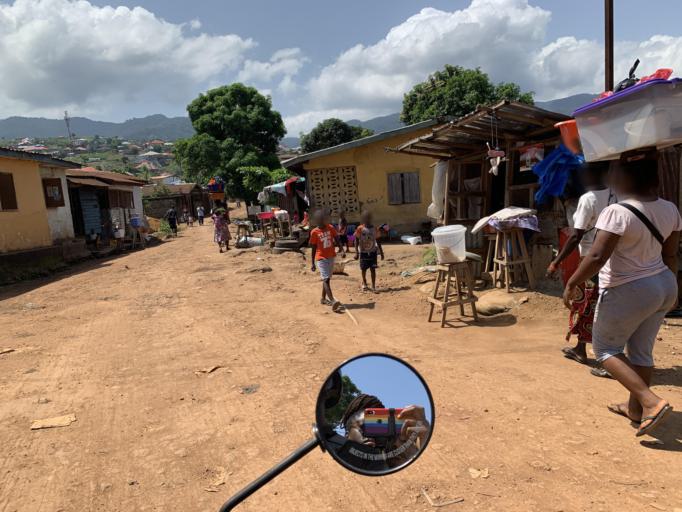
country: SL
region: Western Area
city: Hastings
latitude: 8.3847
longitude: -13.1376
